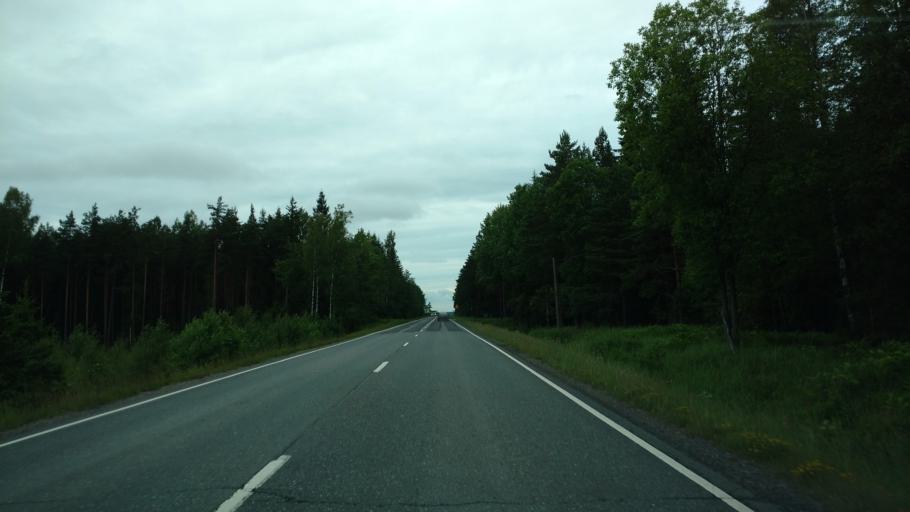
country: FI
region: Varsinais-Suomi
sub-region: Salo
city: Halikko
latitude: 60.4586
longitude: 23.0223
